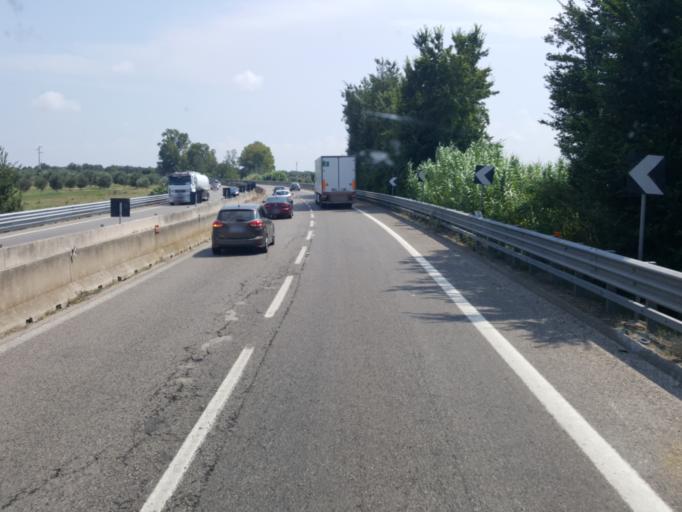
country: IT
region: Apulia
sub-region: Provincia di Brindisi
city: San Pietro Vernotico
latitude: 40.5066
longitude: 18.0243
